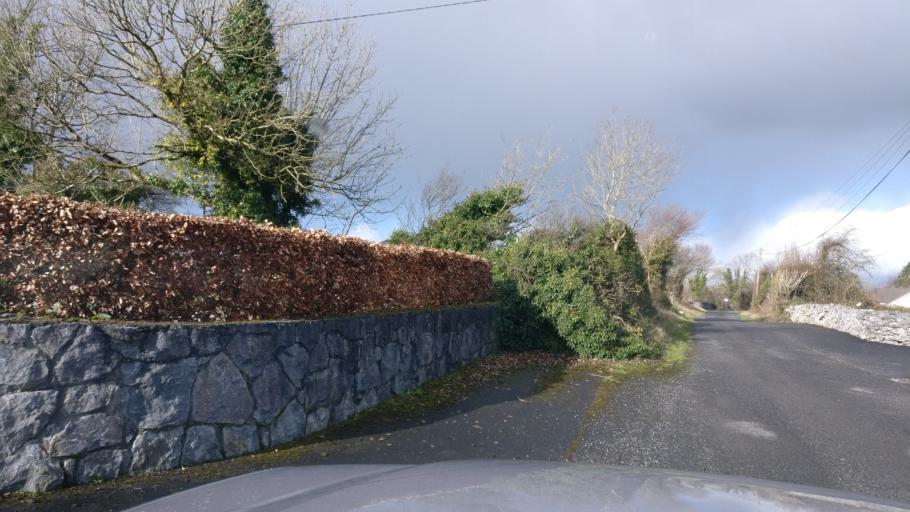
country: IE
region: Connaught
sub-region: County Galway
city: Oranmore
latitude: 53.2371
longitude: -8.8306
